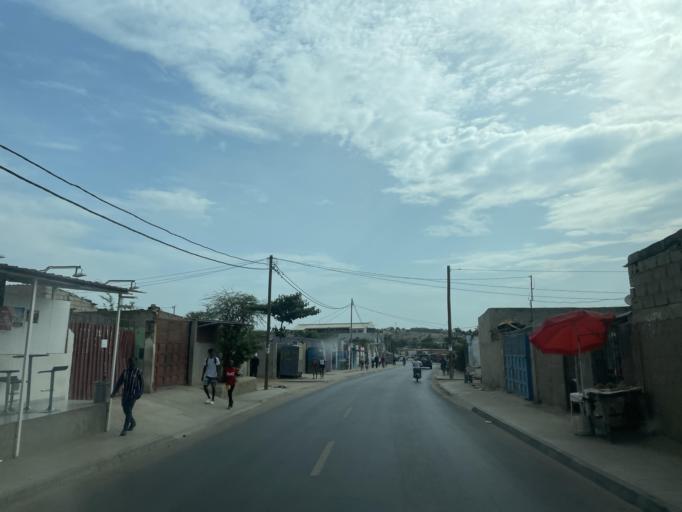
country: AO
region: Luanda
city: Luanda
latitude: -8.9310
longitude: 13.2020
